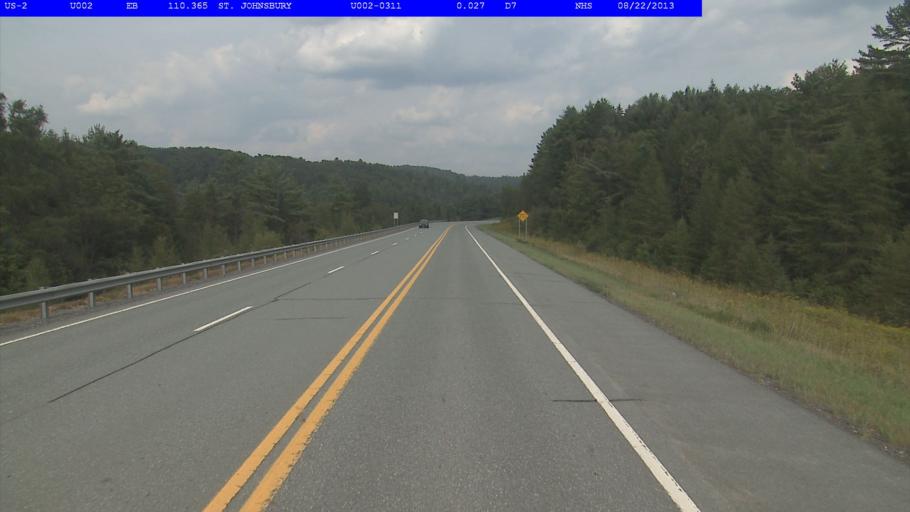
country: US
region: Vermont
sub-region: Caledonia County
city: St Johnsbury
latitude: 44.4433
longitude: -72.0604
